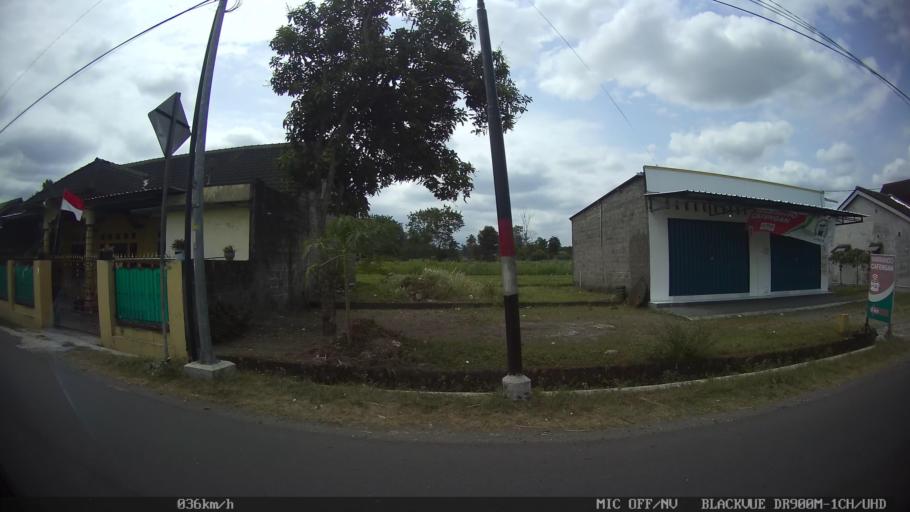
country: ID
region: Central Java
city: Candi Prambanan
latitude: -7.7343
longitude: 110.4754
